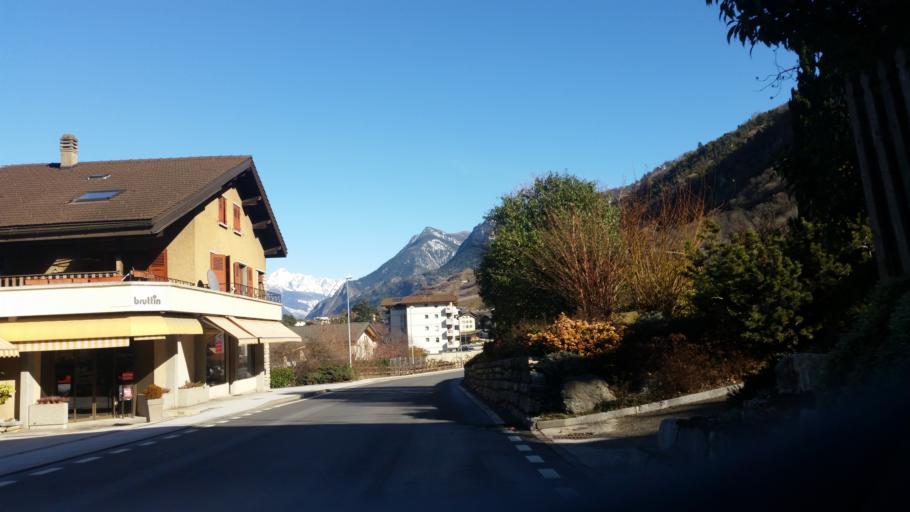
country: CH
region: Valais
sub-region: Sierre District
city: Grone
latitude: 46.2514
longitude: 7.4605
